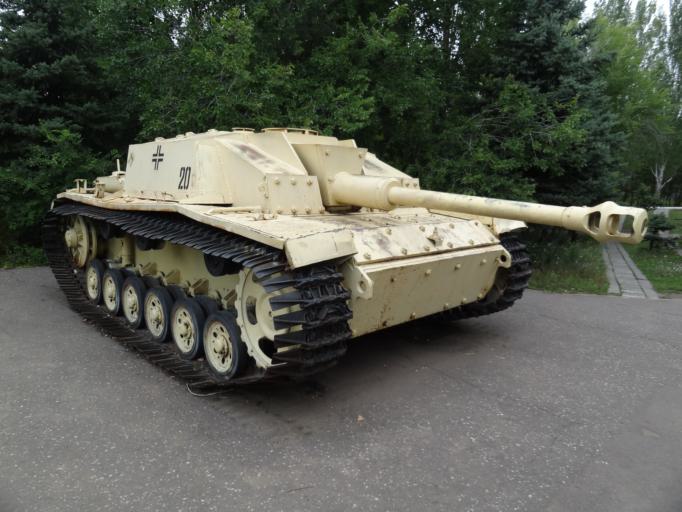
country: RU
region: Saratov
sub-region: Saratovskiy Rayon
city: Saratov
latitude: 51.5430
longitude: 46.0549
